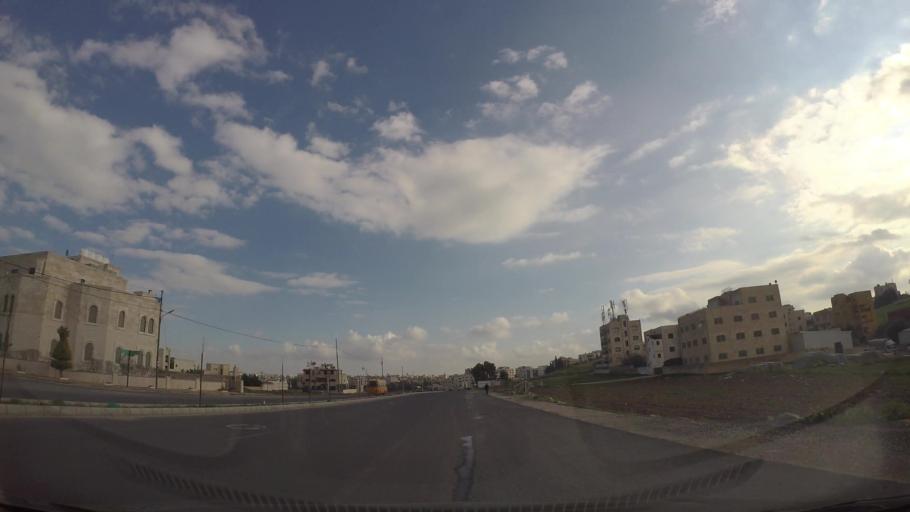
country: JO
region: Amman
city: Umm as Summaq
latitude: 31.9150
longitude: 35.8498
